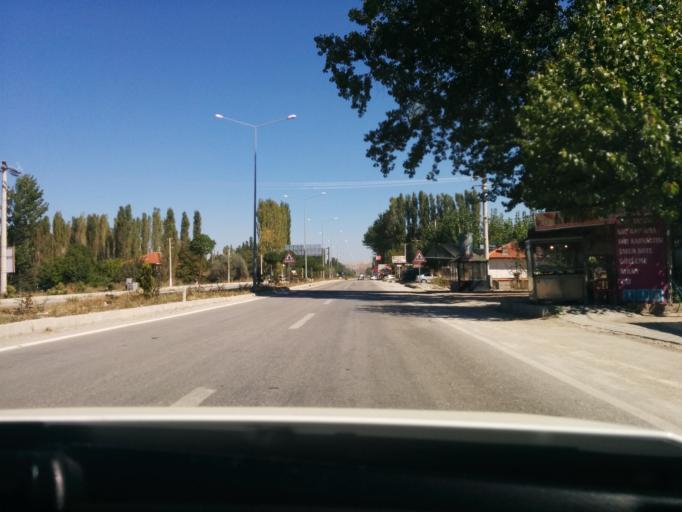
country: TR
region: Antalya
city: Kizilcadag
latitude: 37.0220
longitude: 29.8208
